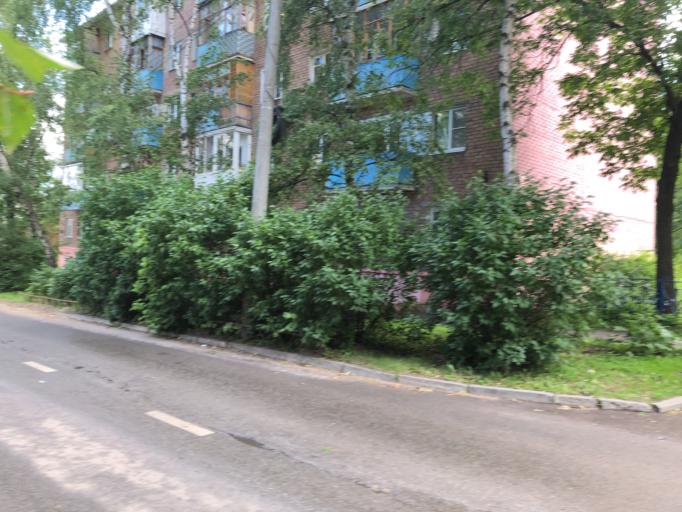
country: RU
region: Jaroslavl
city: Yaroslavl
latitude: 57.6212
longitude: 39.8800
